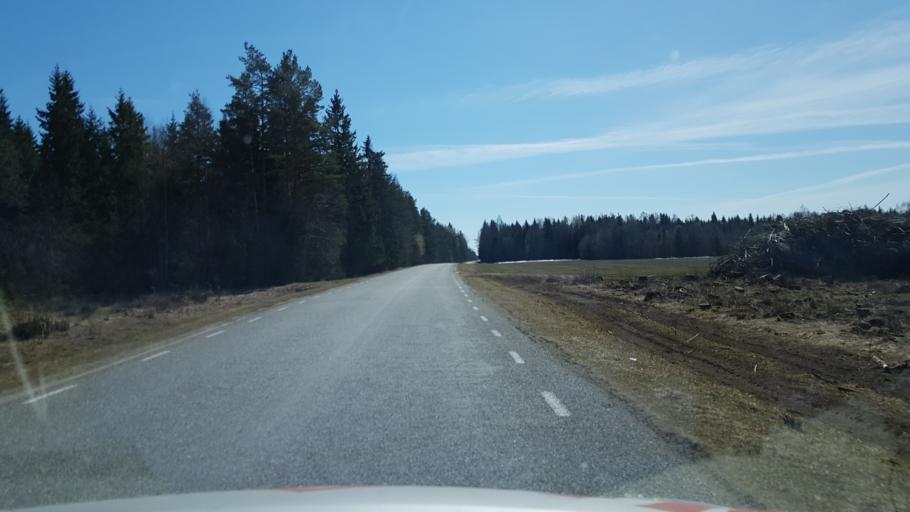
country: EE
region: Laeaene-Virumaa
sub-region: Vinni vald
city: Vinni
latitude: 59.1744
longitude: 26.5051
